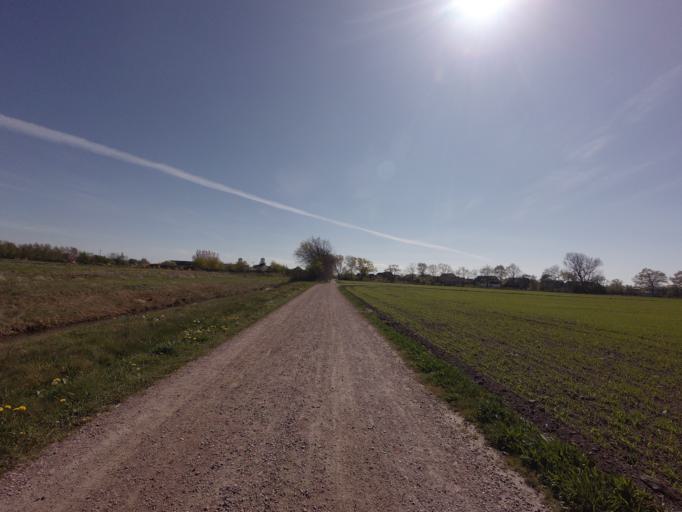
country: SE
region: Skane
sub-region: Hoganas Kommun
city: Hoganas
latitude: 56.1626
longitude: 12.5788
